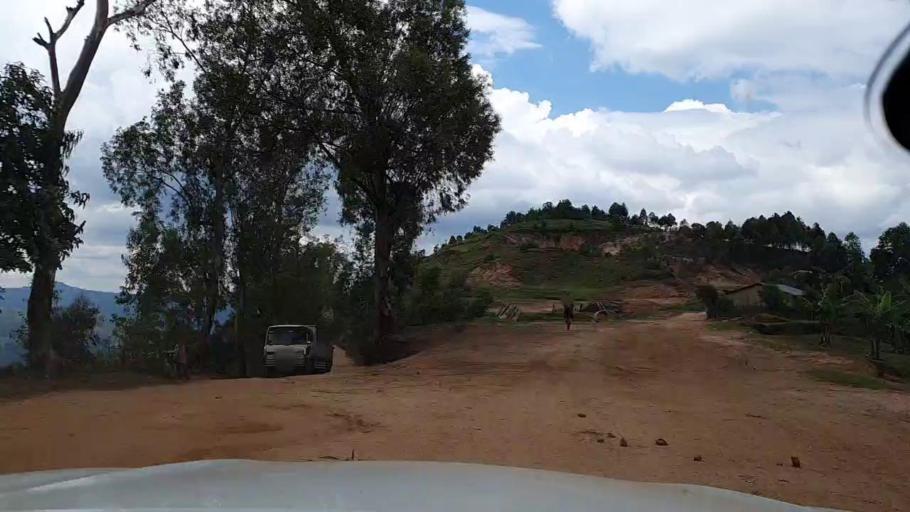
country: RW
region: Southern Province
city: Nzega
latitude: -2.7080
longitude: 29.5142
